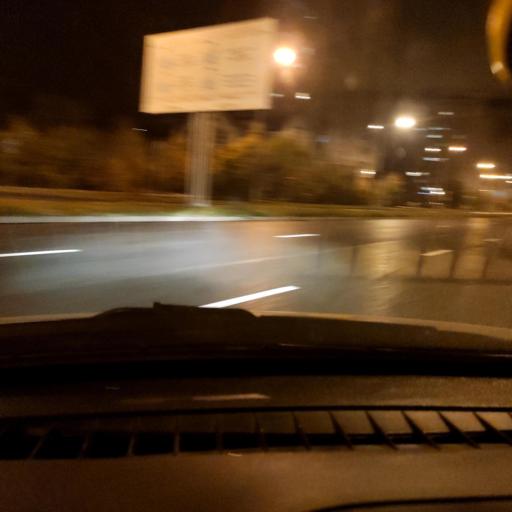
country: RU
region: Samara
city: Tol'yatti
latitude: 53.5142
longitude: 49.2850
